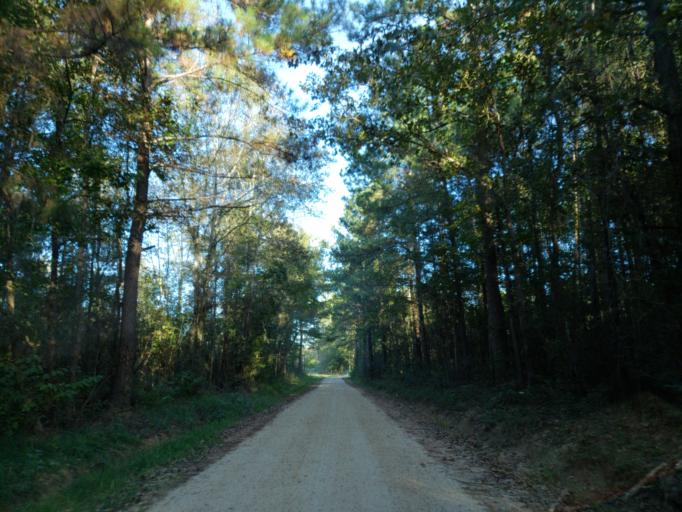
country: US
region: Mississippi
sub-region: Perry County
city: Richton
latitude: 31.3524
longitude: -88.8081
